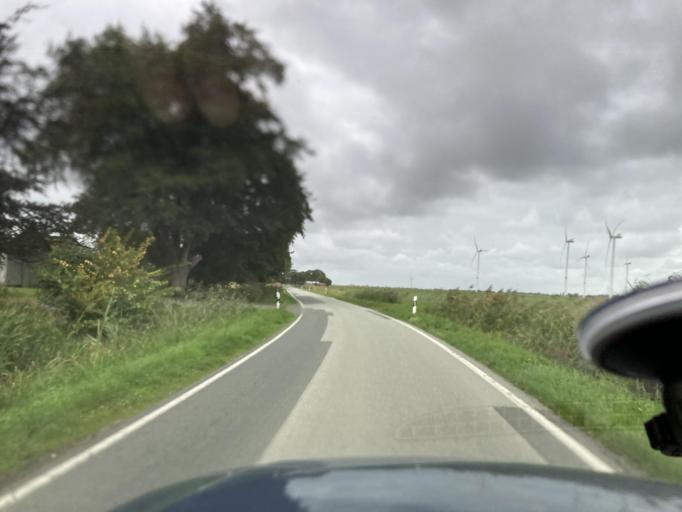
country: DE
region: Schleswig-Holstein
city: Norderwohrden
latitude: 54.1949
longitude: 9.0014
